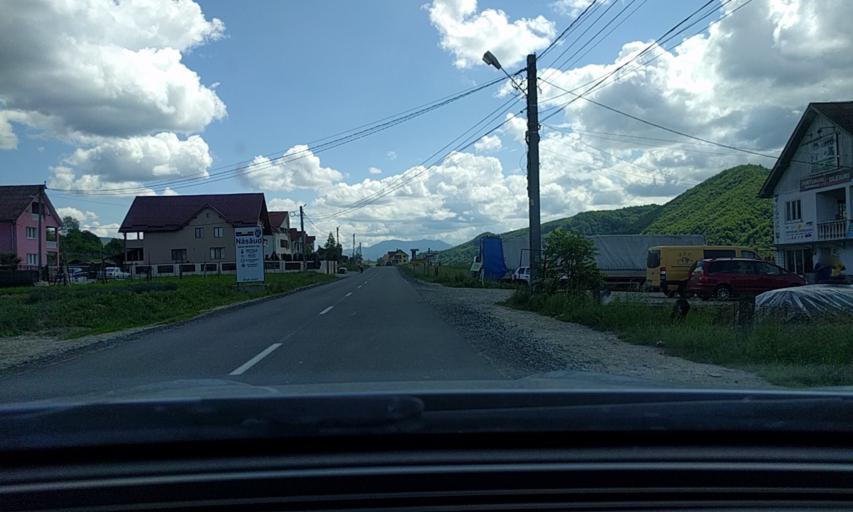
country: RO
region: Bistrita-Nasaud
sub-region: Comuna Rebrisoara
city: Rebrisoara
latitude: 47.2852
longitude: 24.4320
